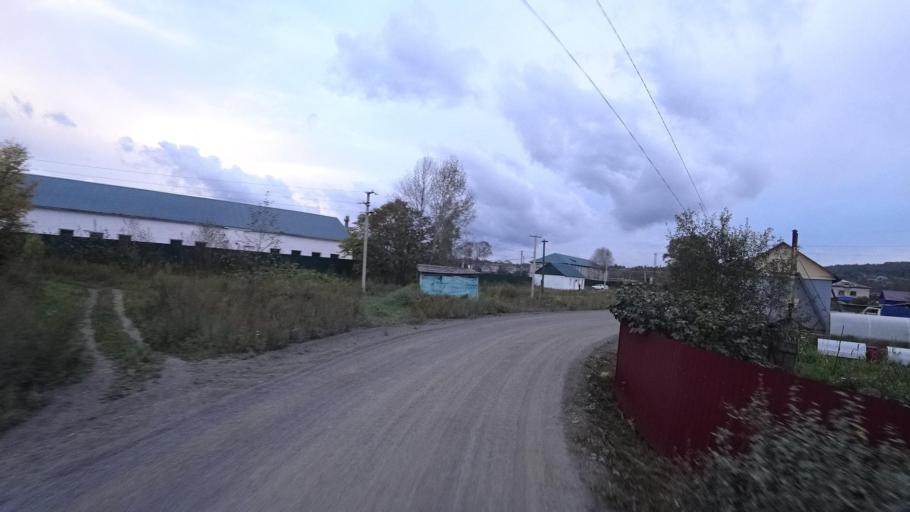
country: RU
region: Jewish Autonomous Oblast
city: Izvestkovyy
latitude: 48.9888
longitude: 131.5531
